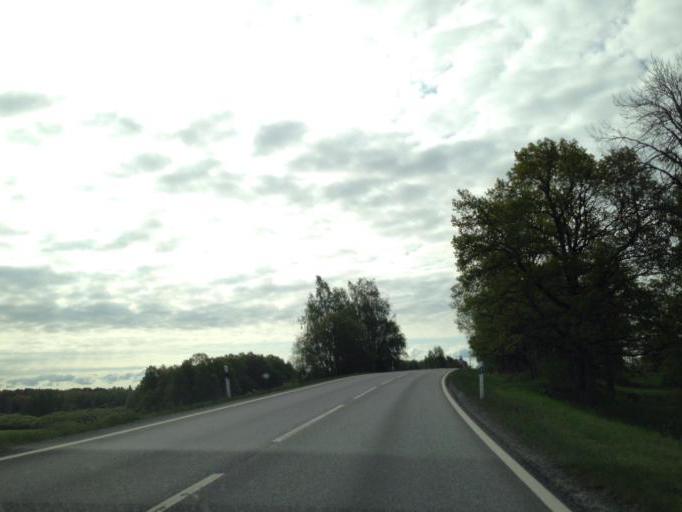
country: SE
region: Soedermanland
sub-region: Flens Kommun
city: Malmkoping
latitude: 59.1006
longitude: 16.7945
